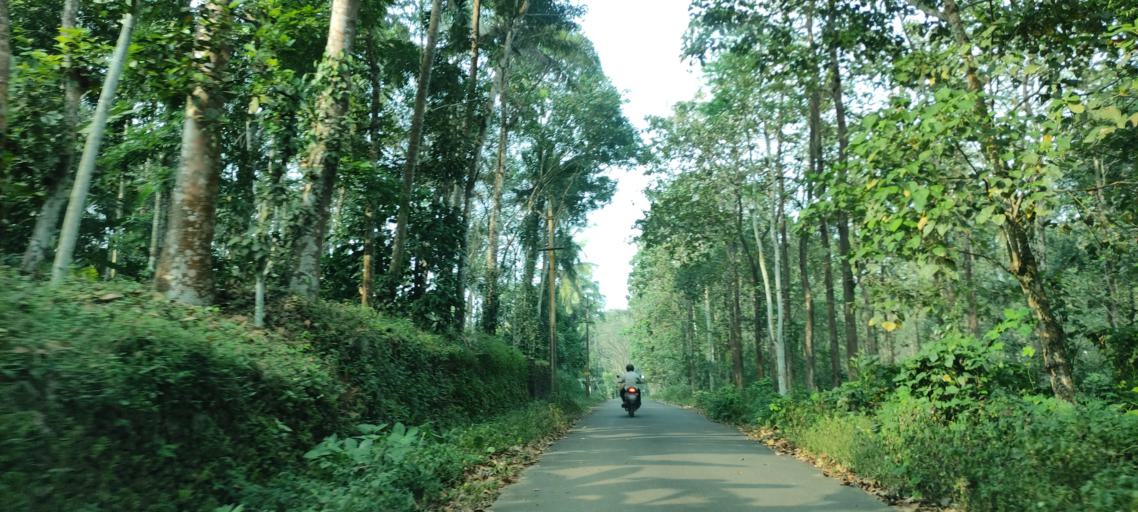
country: IN
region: Kerala
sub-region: Ernakulam
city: Piravam
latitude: 9.8152
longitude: 76.5254
